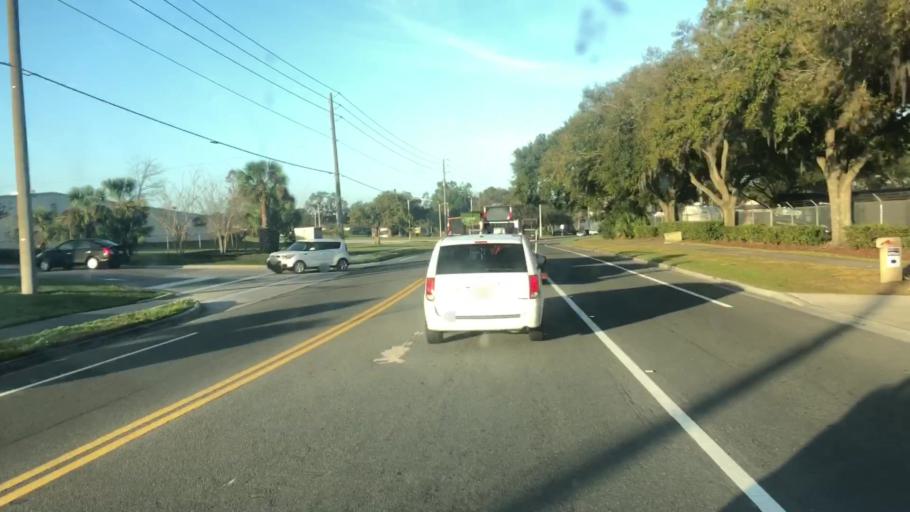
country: US
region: Florida
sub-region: Polk County
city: Gibsonia
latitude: 28.0986
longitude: -81.9747
